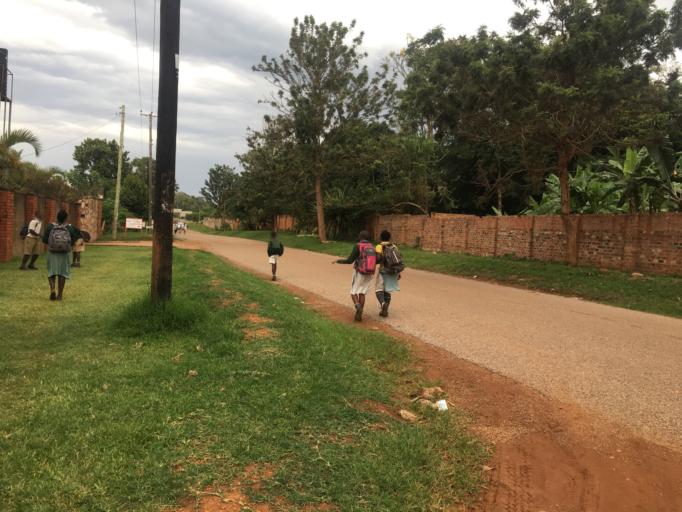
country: UG
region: Central Region
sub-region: Wakiso District
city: Entebbe
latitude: 0.0500
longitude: 32.4639
